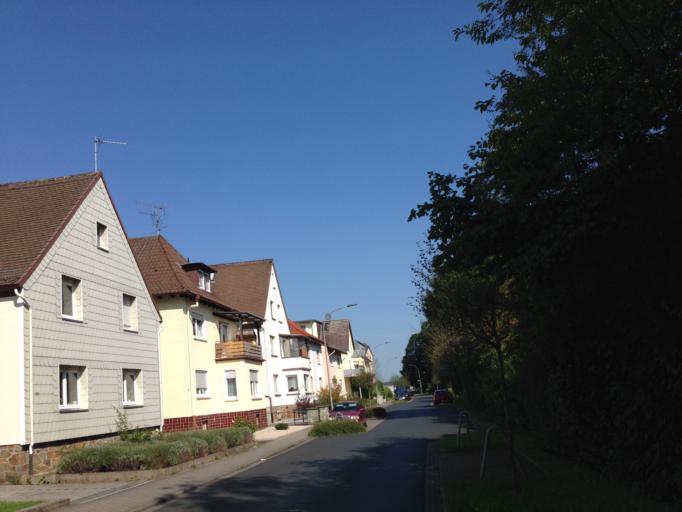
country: DE
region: Hesse
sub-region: Regierungsbezirk Giessen
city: Langgons
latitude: 50.5294
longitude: 8.6609
